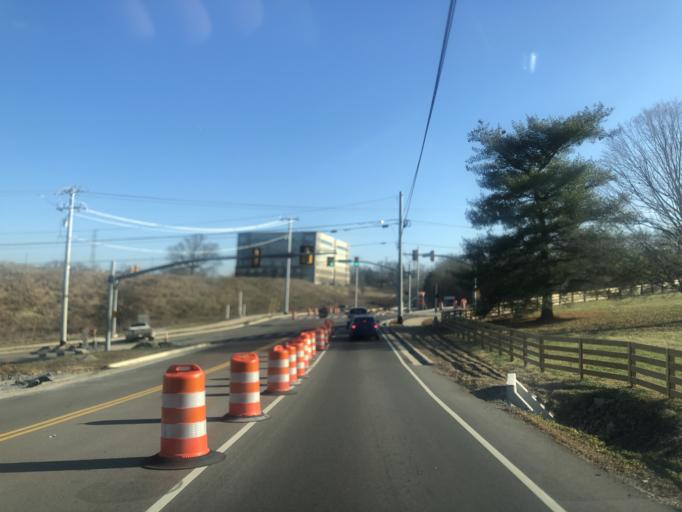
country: US
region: Tennessee
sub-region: Rutherford County
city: La Vergne
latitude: 36.0286
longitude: -86.6496
